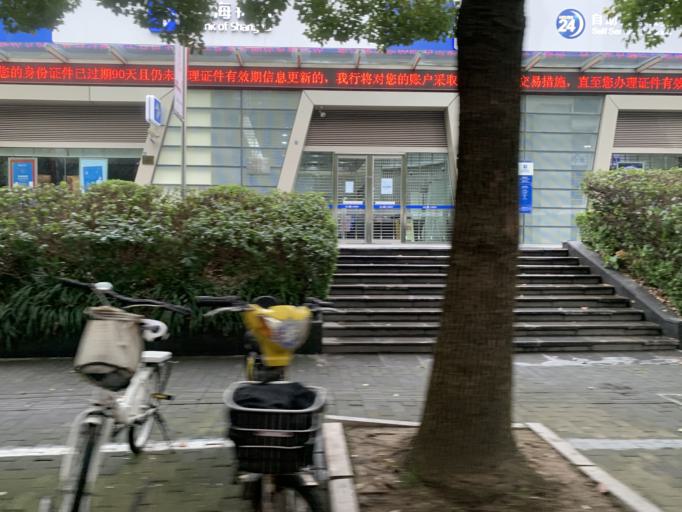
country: CN
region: Shanghai Shi
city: Huamu
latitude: 31.2282
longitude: 121.5561
